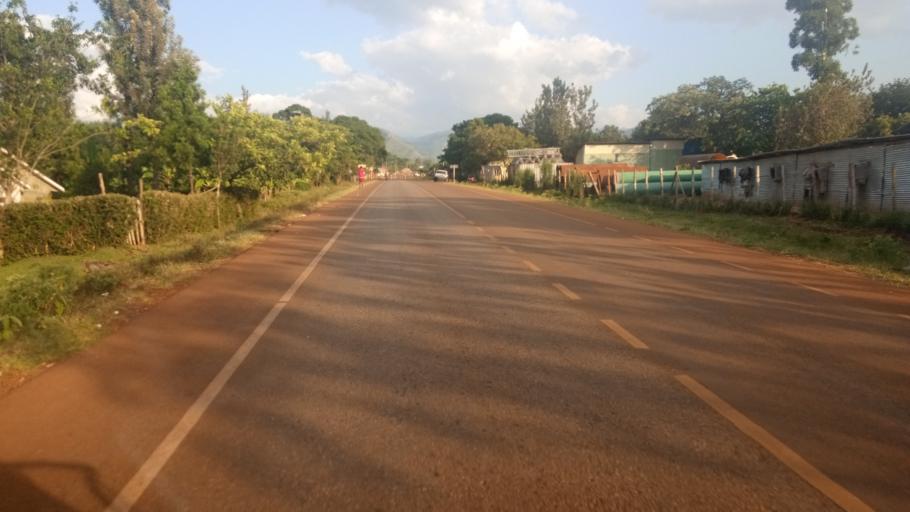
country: UG
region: Eastern Region
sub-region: Sironko District
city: Sironko
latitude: 1.3231
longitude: 34.3330
